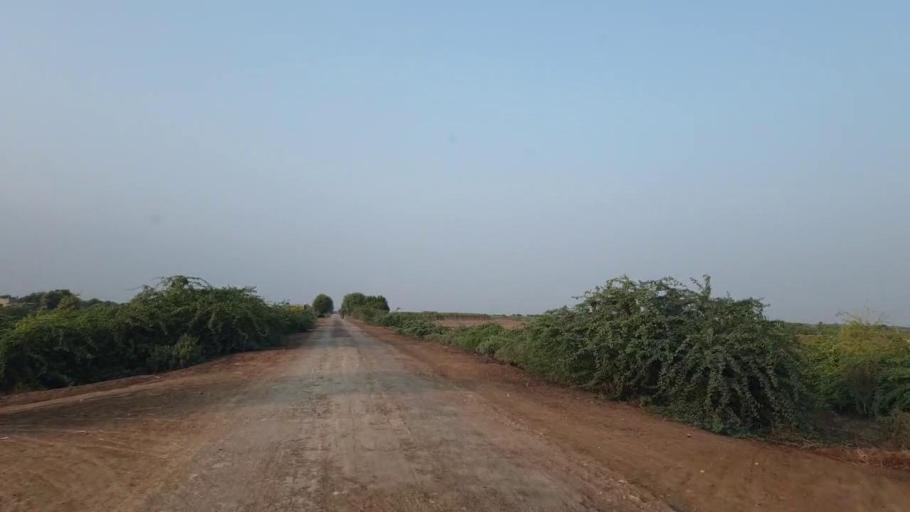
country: PK
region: Sindh
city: Tando Ghulam Ali
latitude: 25.0712
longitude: 68.9595
